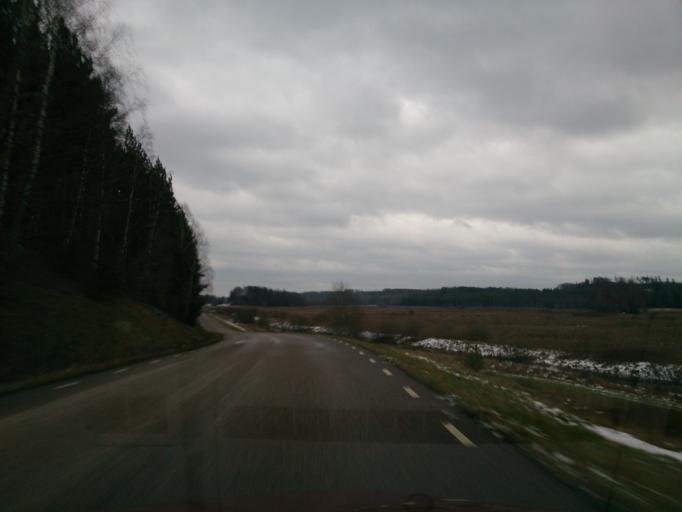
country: SE
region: OEstergoetland
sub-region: Atvidabergs Kommun
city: Atvidaberg
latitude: 58.2900
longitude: 16.0077
